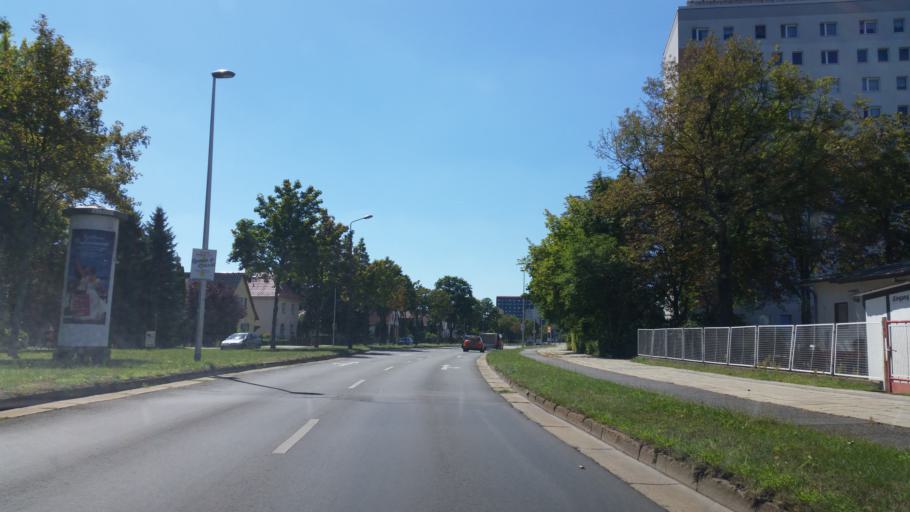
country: DE
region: Brandenburg
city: Cottbus
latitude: 51.7340
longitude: 14.3255
